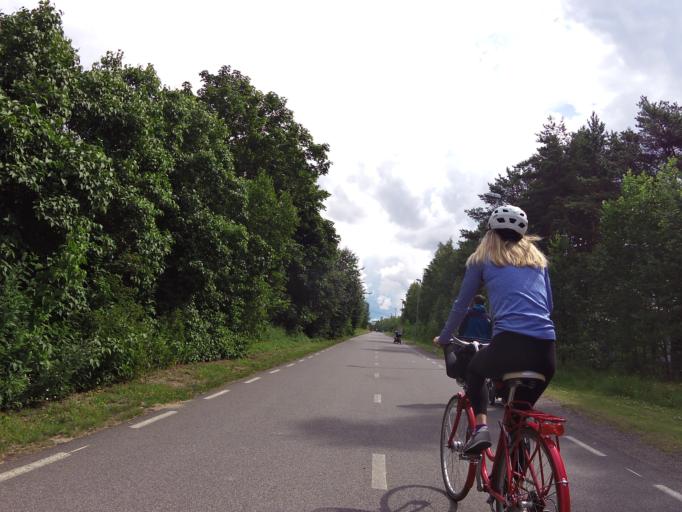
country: EE
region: Harju
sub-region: Saue vald
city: Laagri
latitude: 59.3835
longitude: 24.6505
